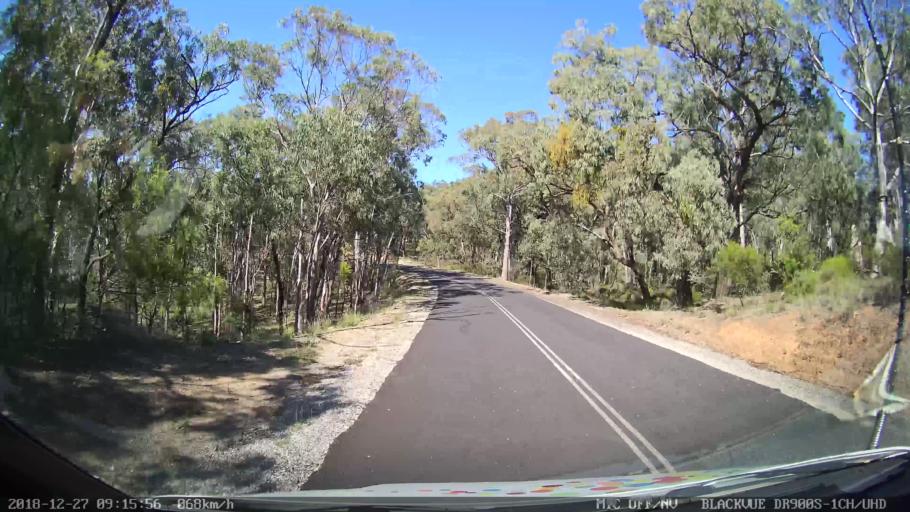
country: AU
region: New South Wales
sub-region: Lithgow
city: Portland
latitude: -33.1349
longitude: 150.0664
